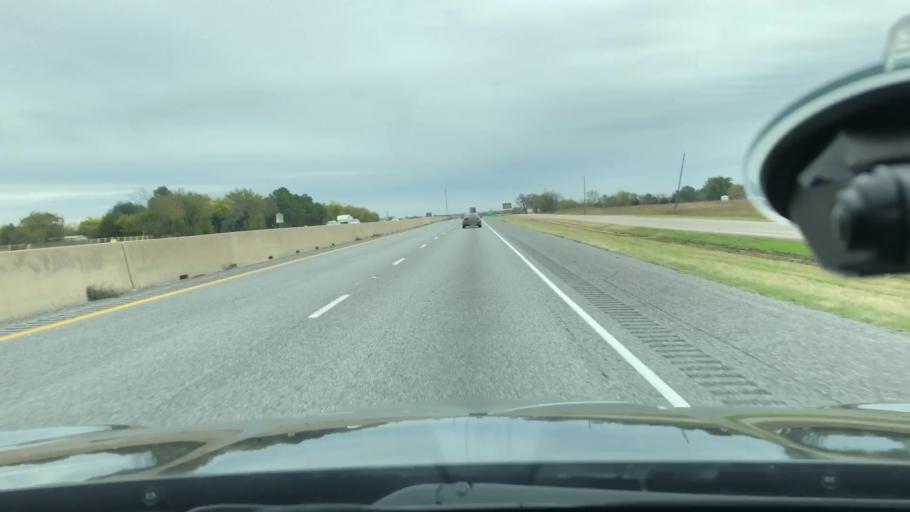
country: US
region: Texas
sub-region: Hunt County
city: Commerce
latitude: 33.1303
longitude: -95.9622
